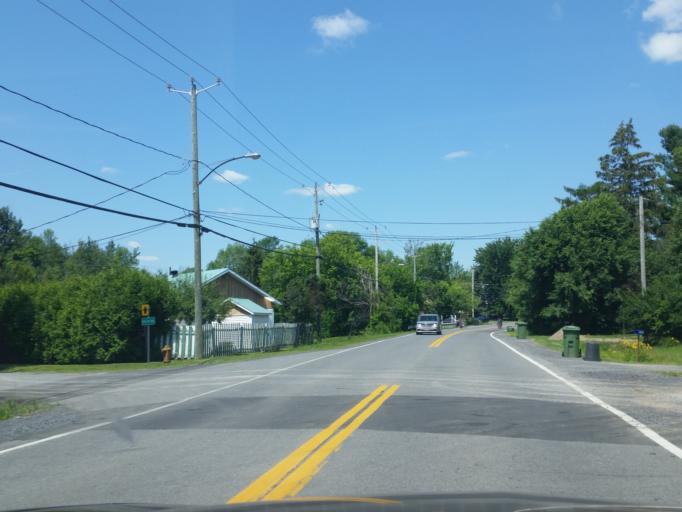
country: CA
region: Quebec
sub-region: Monteregie
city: Richelieu
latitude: 45.4339
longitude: -73.2523
